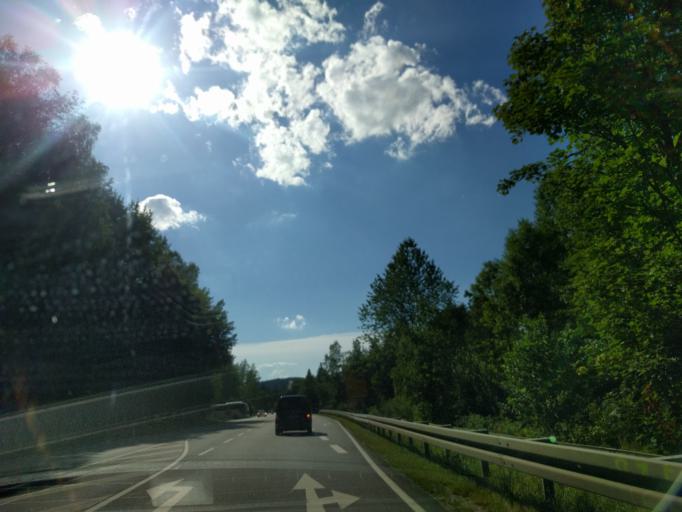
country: DE
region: Bavaria
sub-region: Lower Bavaria
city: Regen
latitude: 48.9658
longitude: 13.1116
